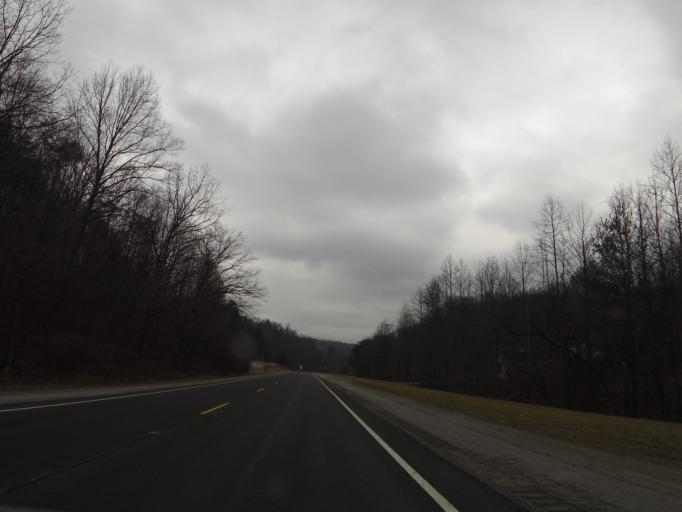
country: US
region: Tennessee
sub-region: Scott County
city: Huntsville
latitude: 36.4100
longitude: -84.4579
